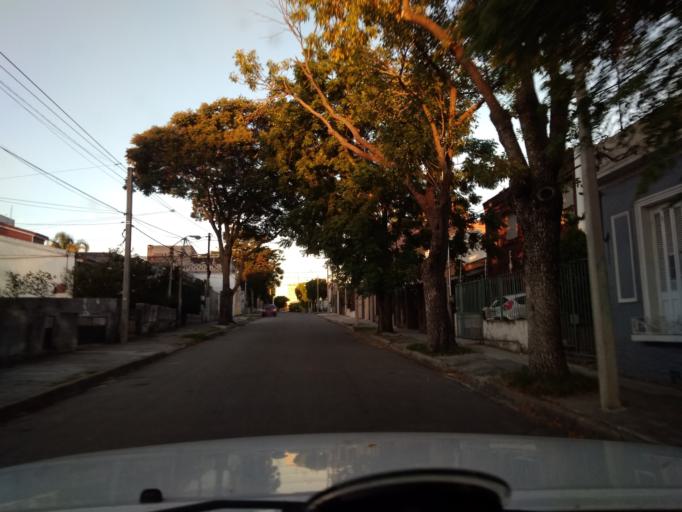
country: UY
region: Montevideo
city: Montevideo
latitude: -34.8938
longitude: -56.1219
